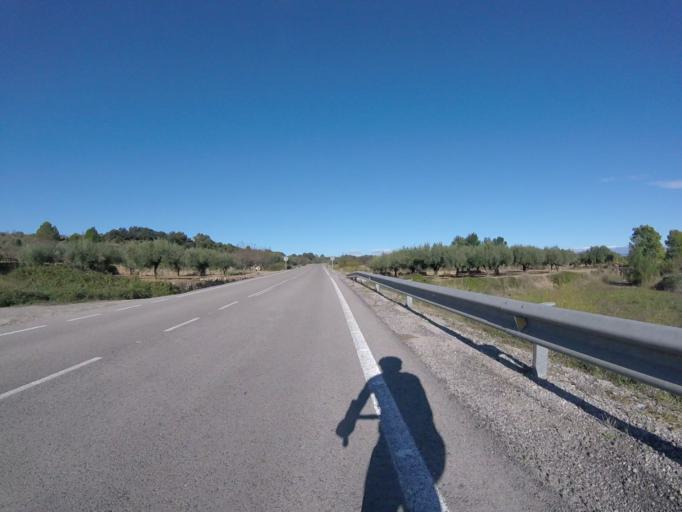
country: ES
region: Valencia
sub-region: Provincia de Castello
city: Cervera del Maestre
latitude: 40.4694
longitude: 0.2452
